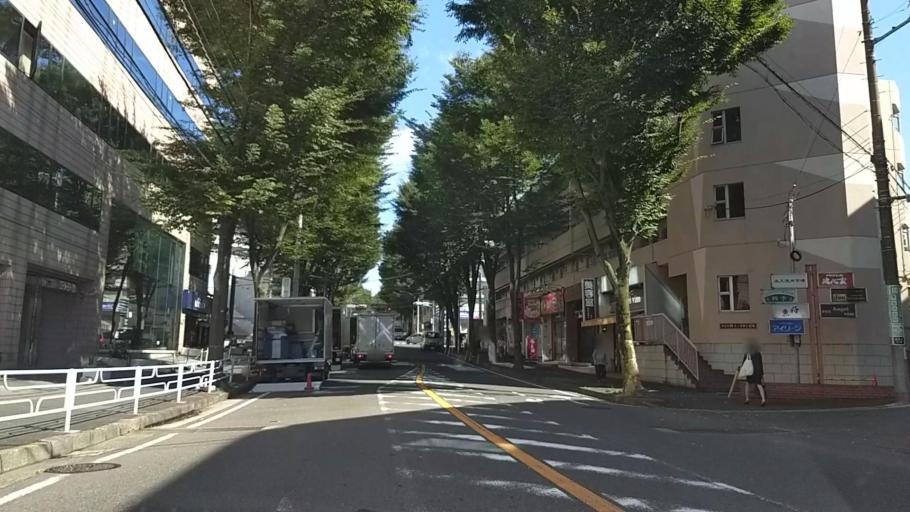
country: JP
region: Tokyo
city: Chofugaoka
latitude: 35.5695
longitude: 139.5544
